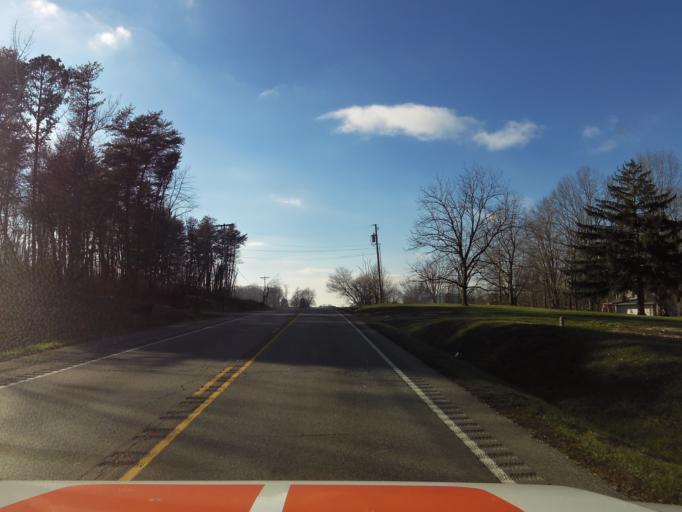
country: US
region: Indiana
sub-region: Jackson County
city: Seymour
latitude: 38.9637
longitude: -85.8244
